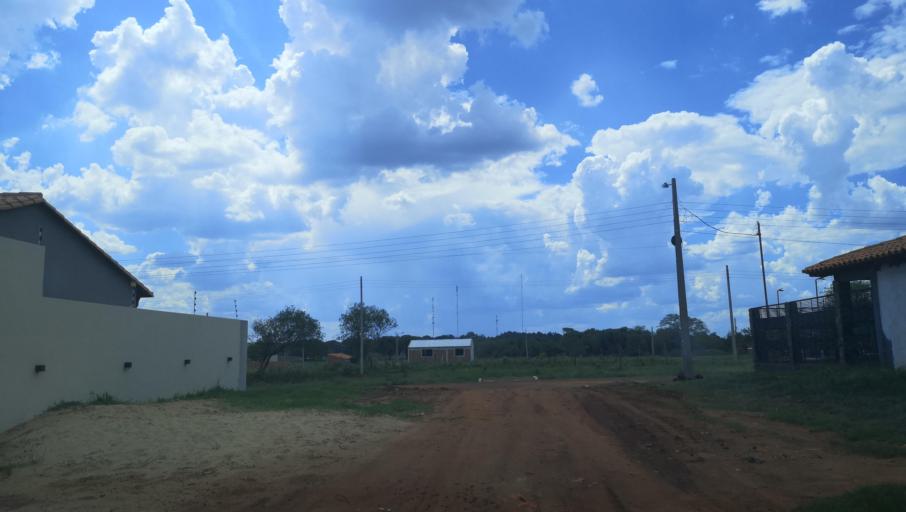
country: PY
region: Misiones
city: Santa Maria
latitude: -26.8964
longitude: -57.0410
